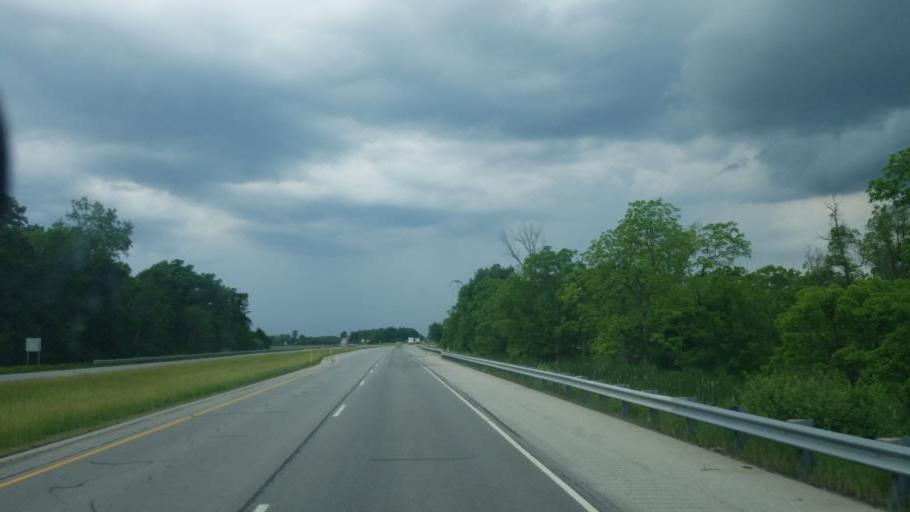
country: US
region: Indiana
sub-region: Whitley County
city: Churubusco
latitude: 41.1253
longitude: -85.2623
